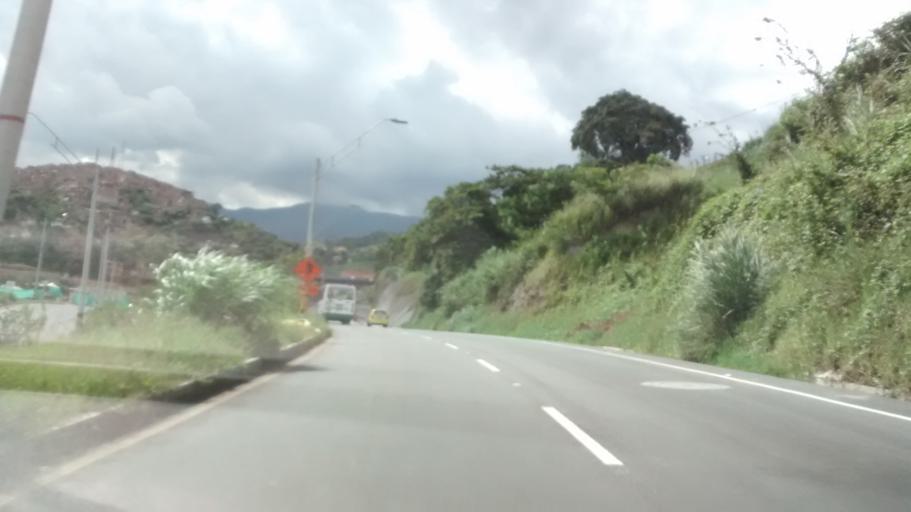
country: CO
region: Antioquia
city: Medellin
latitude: 6.2762
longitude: -75.6028
